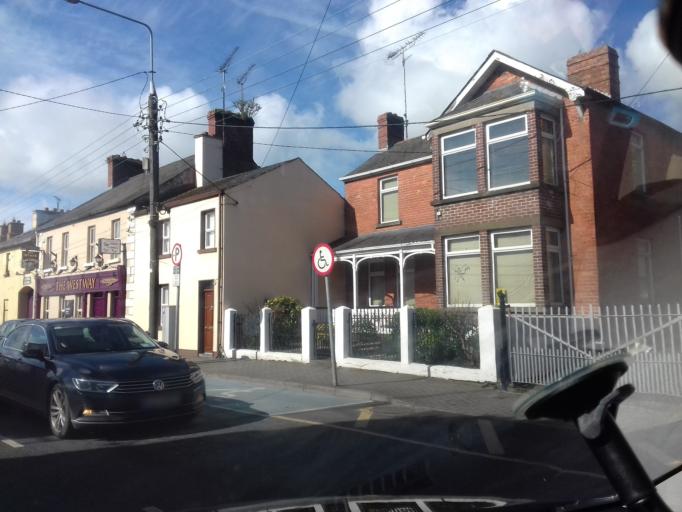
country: IE
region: Leinster
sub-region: An Mhi
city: Kells
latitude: 53.7242
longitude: -6.8804
